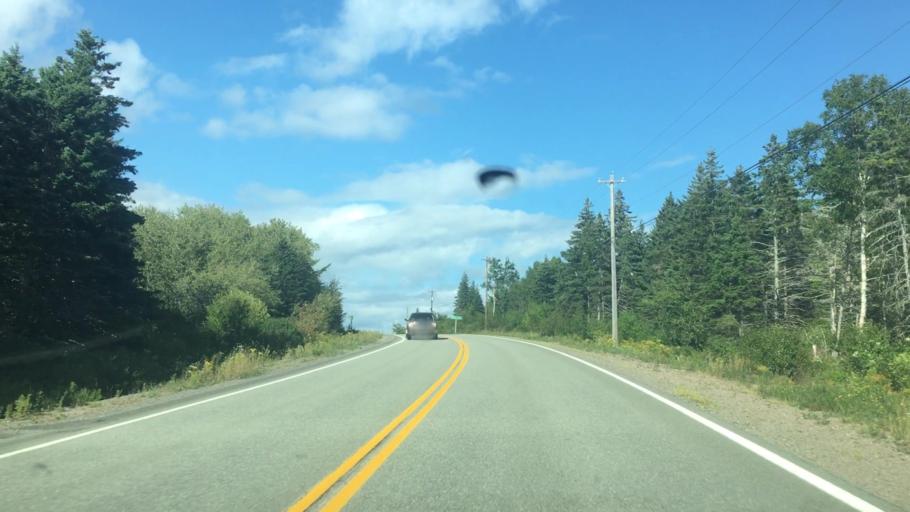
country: CA
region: Nova Scotia
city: Sydney
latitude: 45.8545
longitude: -60.6308
